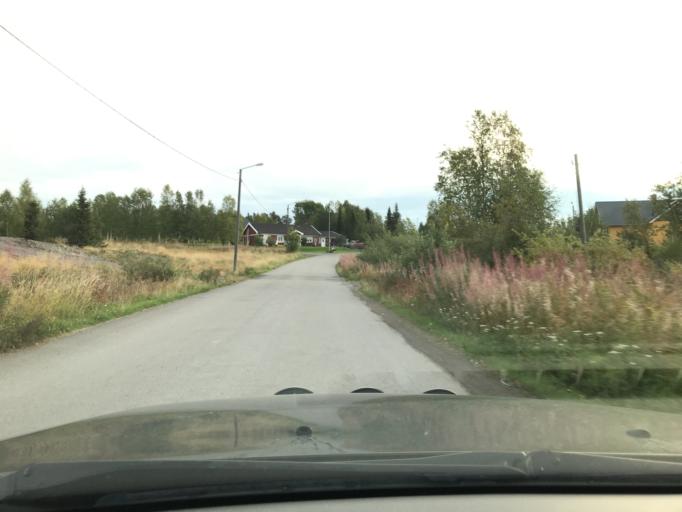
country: SE
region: Norrbotten
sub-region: Gallivare Kommun
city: Malmberget
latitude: 67.6458
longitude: 21.0622
